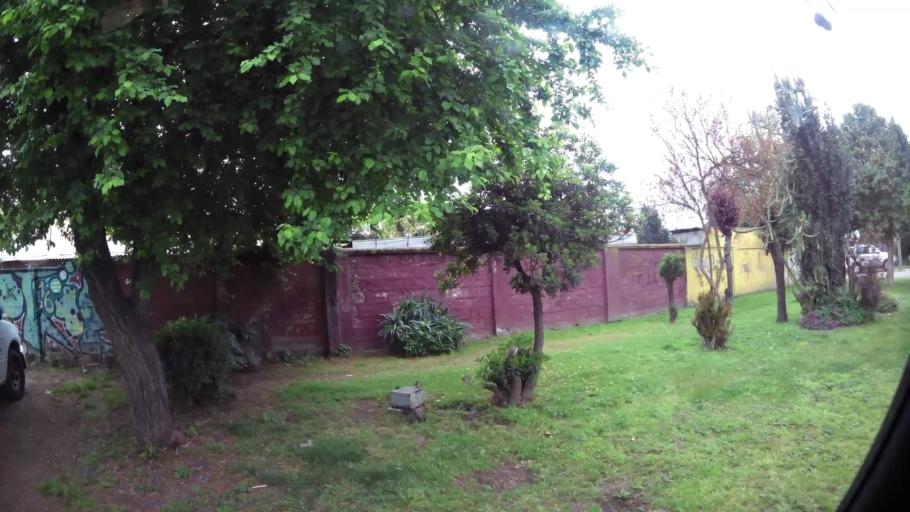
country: CL
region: Santiago Metropolitan
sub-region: Provincia de Santiago
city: Lo Prado
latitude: -33.5019
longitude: -70.7730
